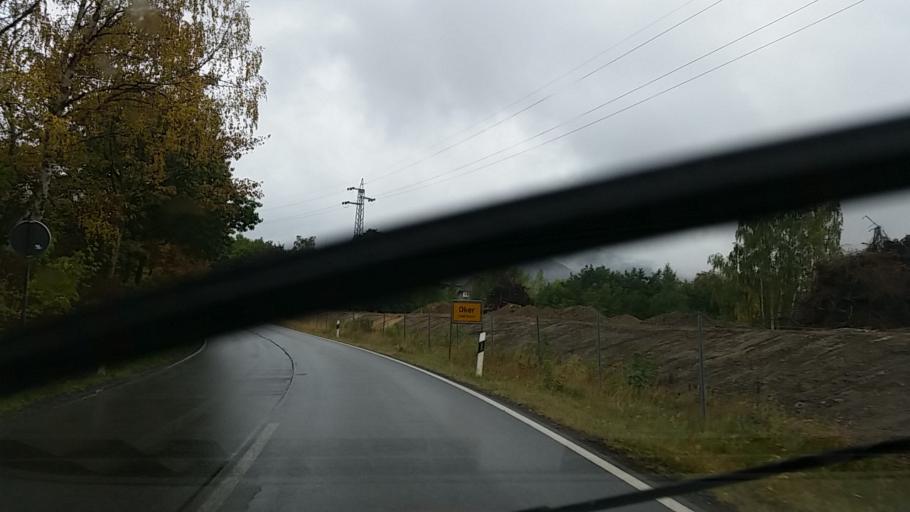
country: DE
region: Lower Saxony
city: Goslar
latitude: 51.9126
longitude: 10.4871
